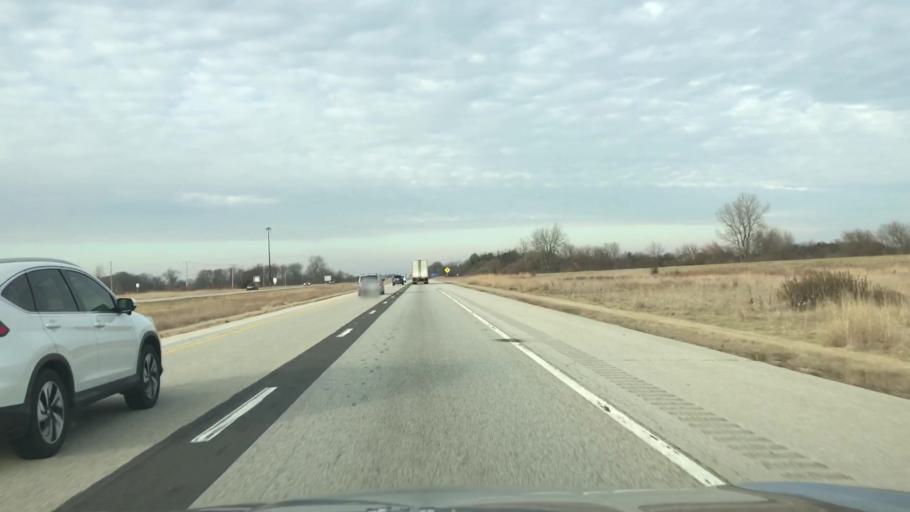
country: US
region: Illinois
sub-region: Sangamon County
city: Divernon
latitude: 39.5686
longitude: -89.6460
